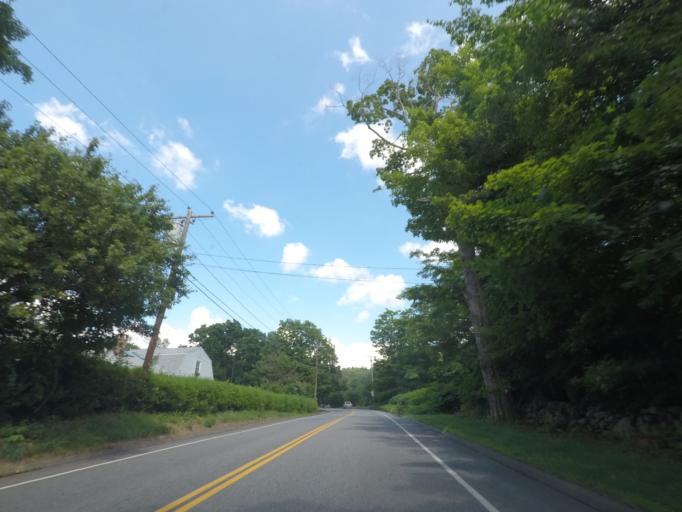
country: US
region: Massachusetts
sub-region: Hampden County
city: Monson Center
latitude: 42.1139
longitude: -72.2944
